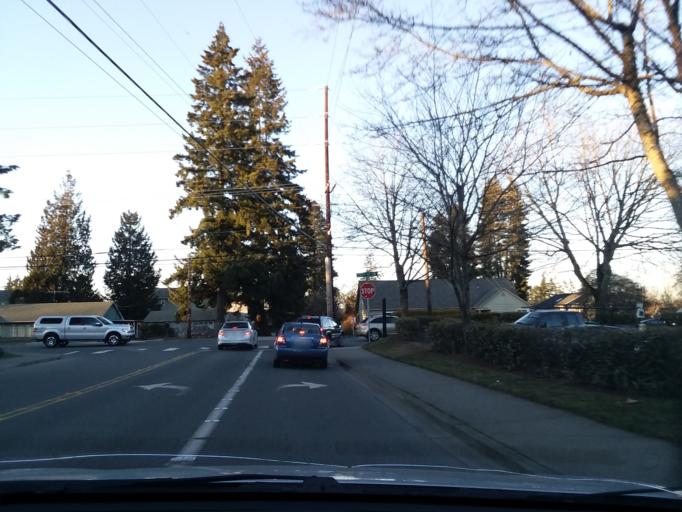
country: US
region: Washington
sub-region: Snohomish County
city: Mountlake Terrace
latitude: 47.8061
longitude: -122.2977
